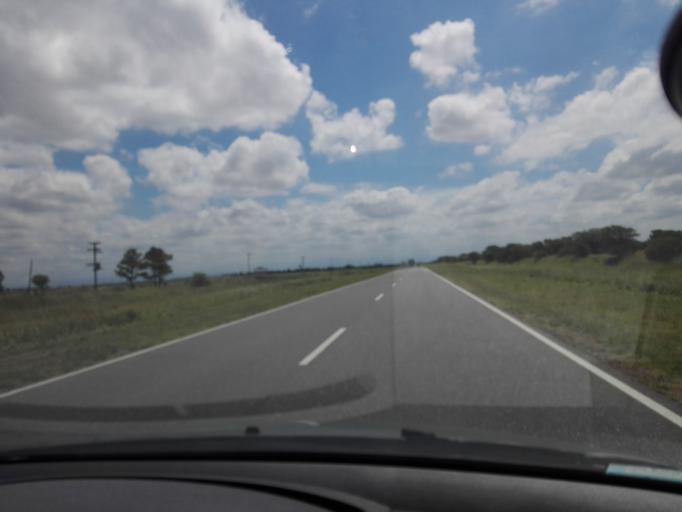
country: AR
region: Cordoba
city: Toledo
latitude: -31.6466
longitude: -64.0530
